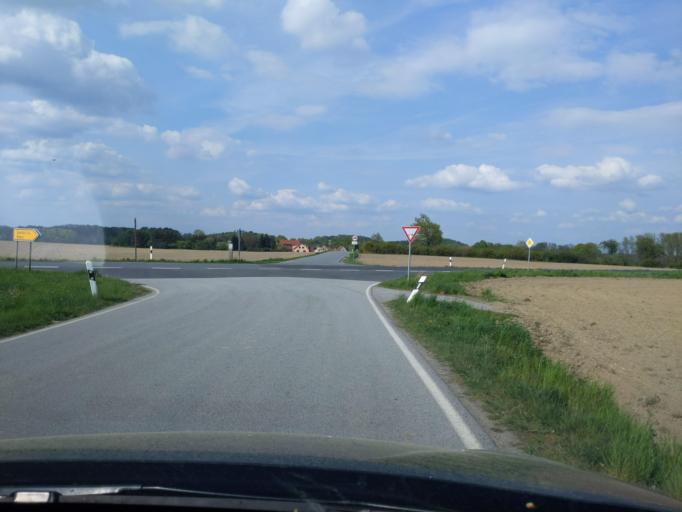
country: DE
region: Saxony
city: Kubschutz
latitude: 51.1944
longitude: 14.4966
